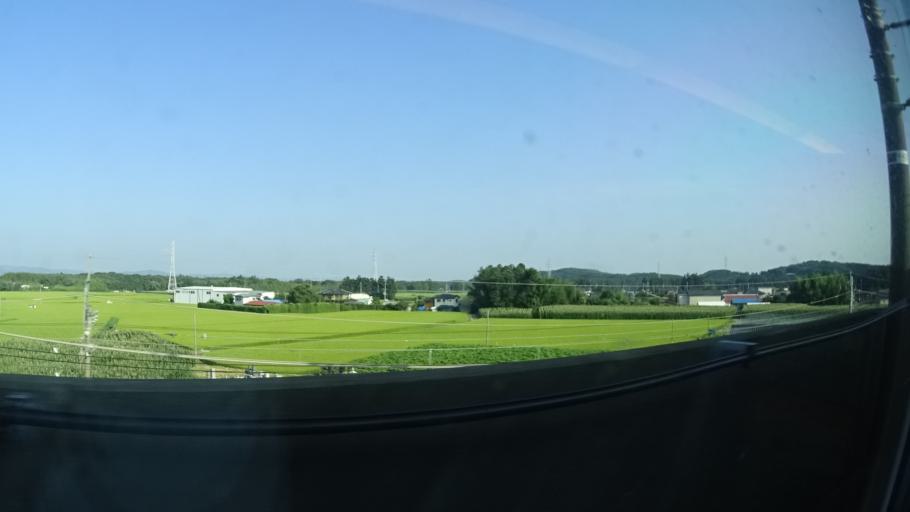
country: JP
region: Tochigi
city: Otawara
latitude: 36.9089
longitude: 140.0041
